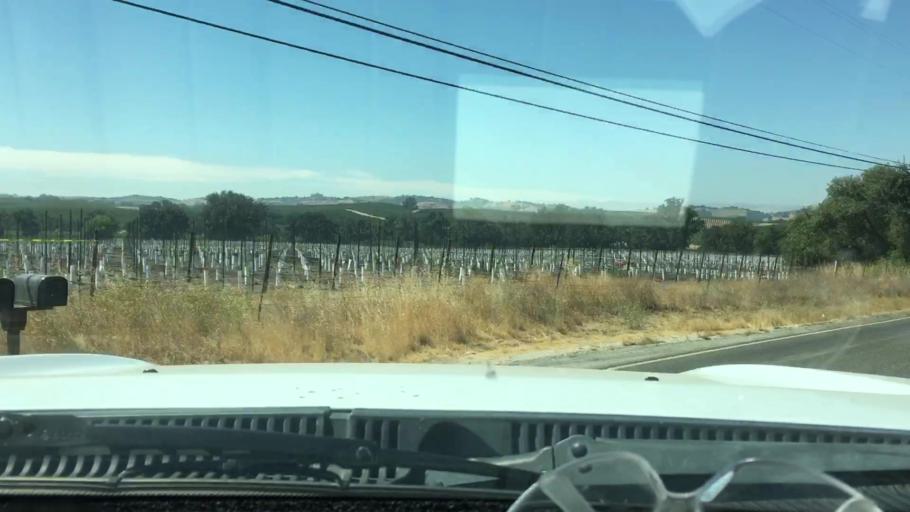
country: US
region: California
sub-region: San Luis Obispo County
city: Paso Robles
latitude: 35.5964
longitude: -120.6363
